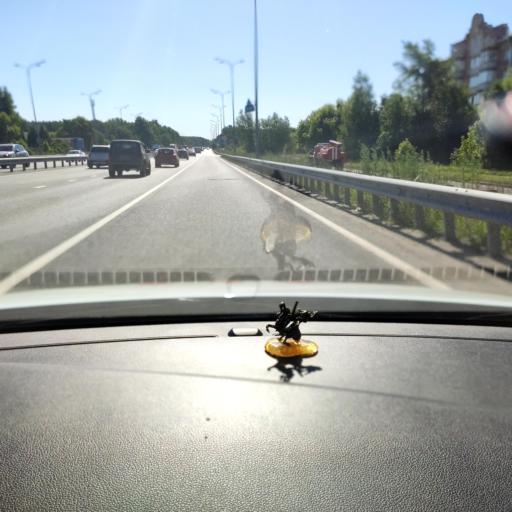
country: RU
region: Tatarstan
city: Osinovo
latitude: 55.8477
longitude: 48.9089
